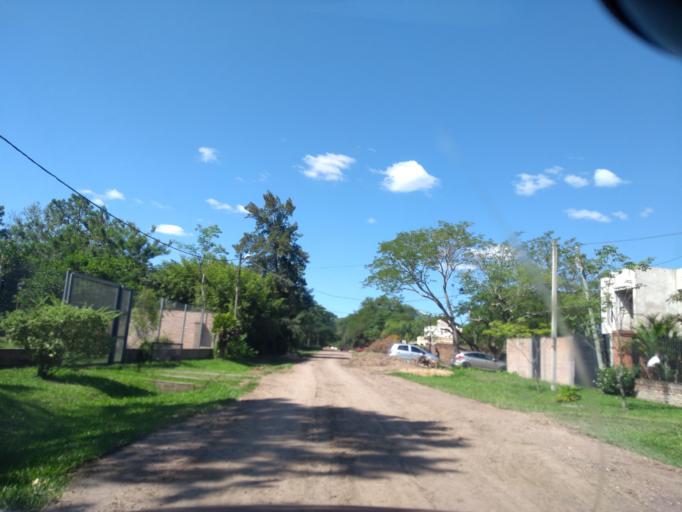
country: AR
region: Chaco
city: Resistencia
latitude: -27.4221
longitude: -58.9455
